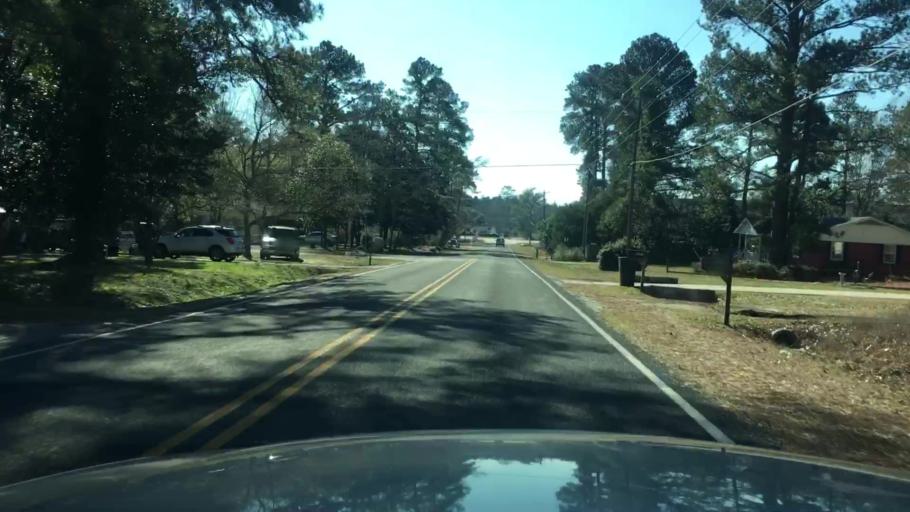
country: US
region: North Carolina
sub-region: Cumberland County
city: Hope Mills
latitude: 34.9966
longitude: -78.9653
